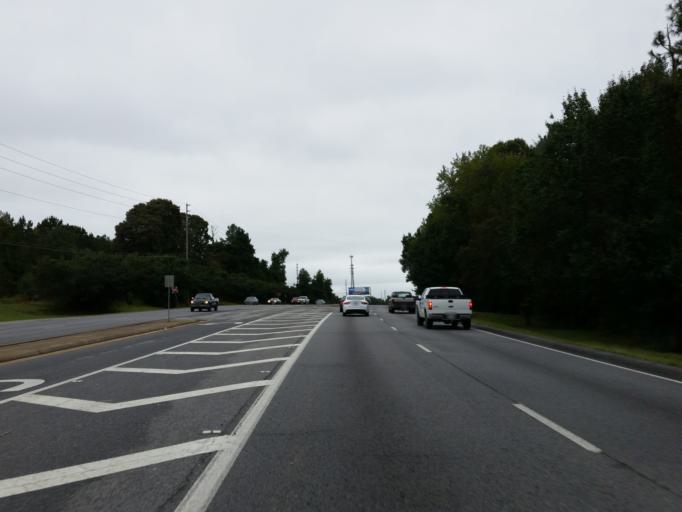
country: US
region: Georgia
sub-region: Clayton County
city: Bonanza
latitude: 33.4576
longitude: -84.3279
